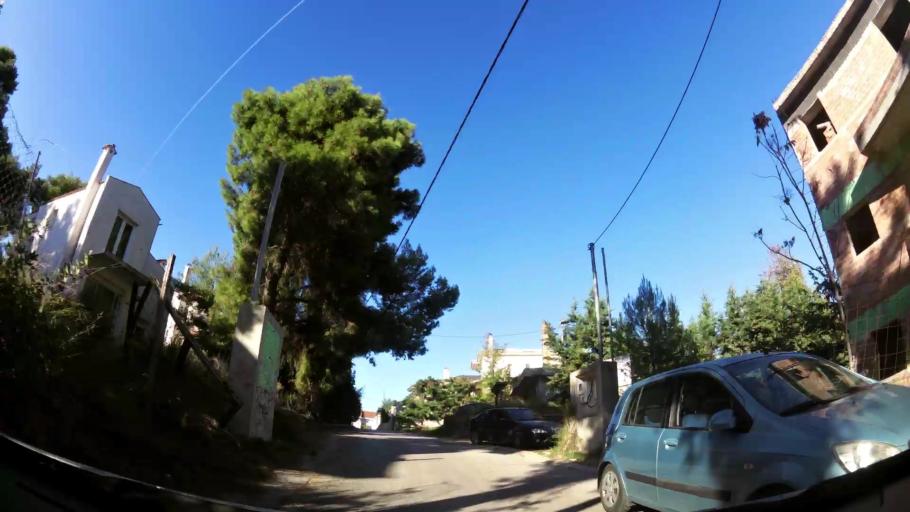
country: GR
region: Attica
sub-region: Nomarchia Anatolikis Attikis
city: Agios Stefanos
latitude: 38.1381
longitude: 23.8489
